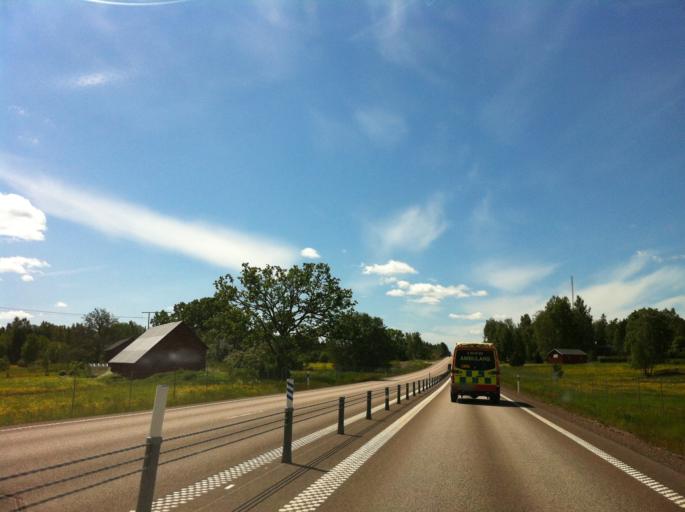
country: SE
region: Vaestra Goetaland
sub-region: Melleruds Kommun
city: Mellerud
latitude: 58.8541
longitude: 12.5550
